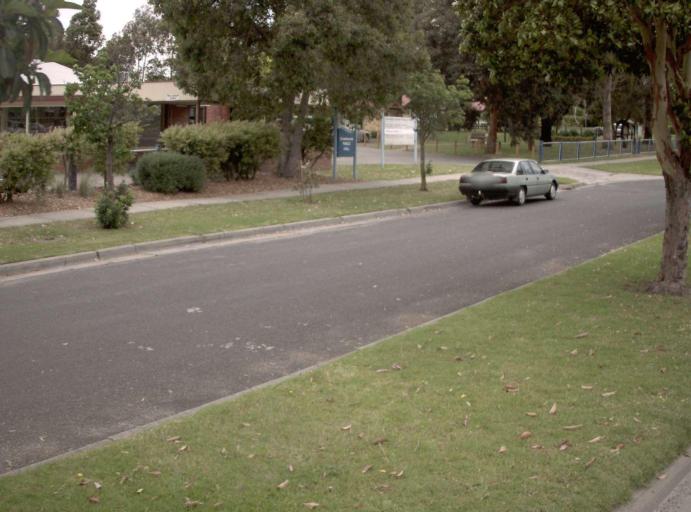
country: AU
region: Victoria
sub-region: Casey
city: Cranbourne
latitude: -38.1060
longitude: 145.2822
